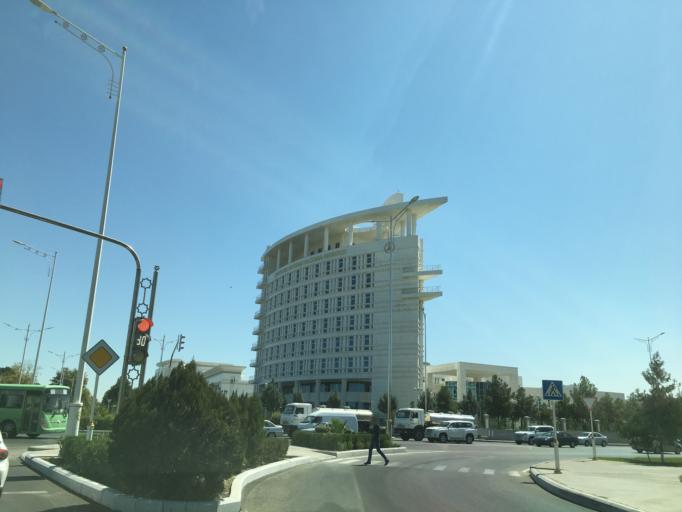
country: TM
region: Ahal
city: Ashgabat
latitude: 37.9521
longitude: 58.3387
